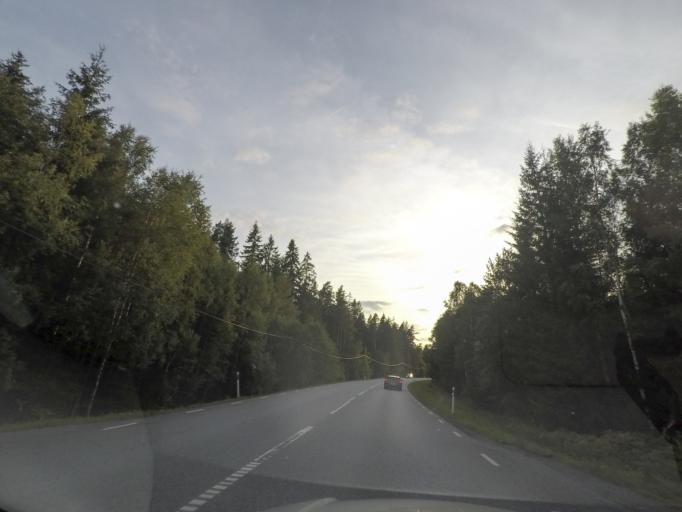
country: SE
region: OErebro
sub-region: Nora Kommun
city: As
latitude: 59.5188
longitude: 14.9338
